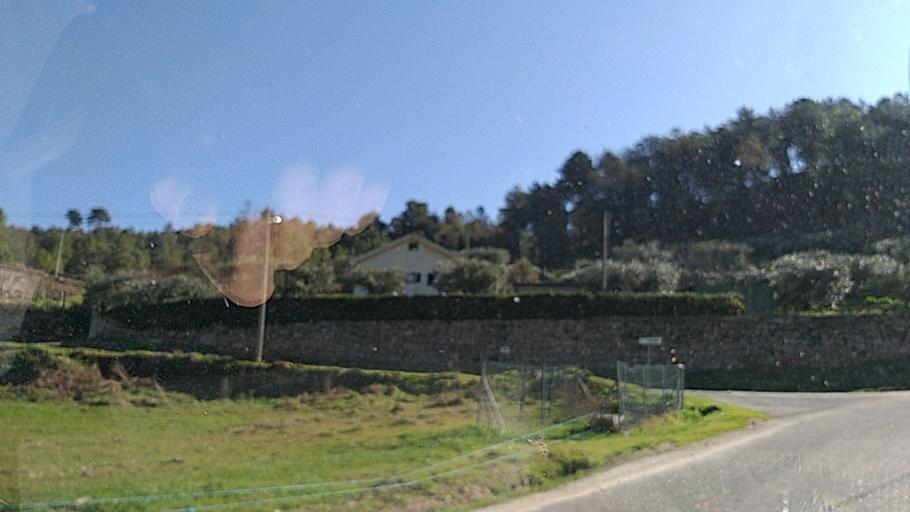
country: PT
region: Guarda
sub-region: Celorico da Beira
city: Celorico da Beira
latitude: 40.6881
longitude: -7.4004
